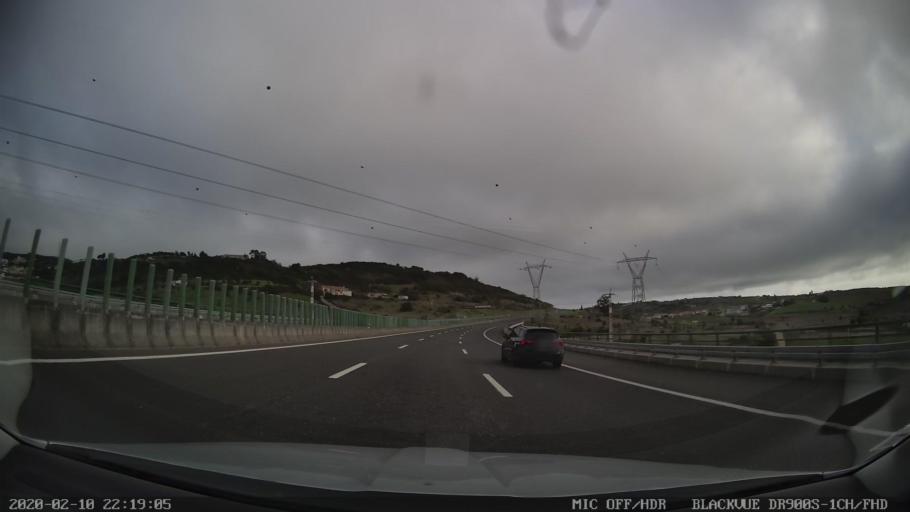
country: PT
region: Lisbon
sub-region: Arruda Dos Vinhos
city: Arruda dos Vinhos
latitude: 38.9502
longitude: -9.0671
